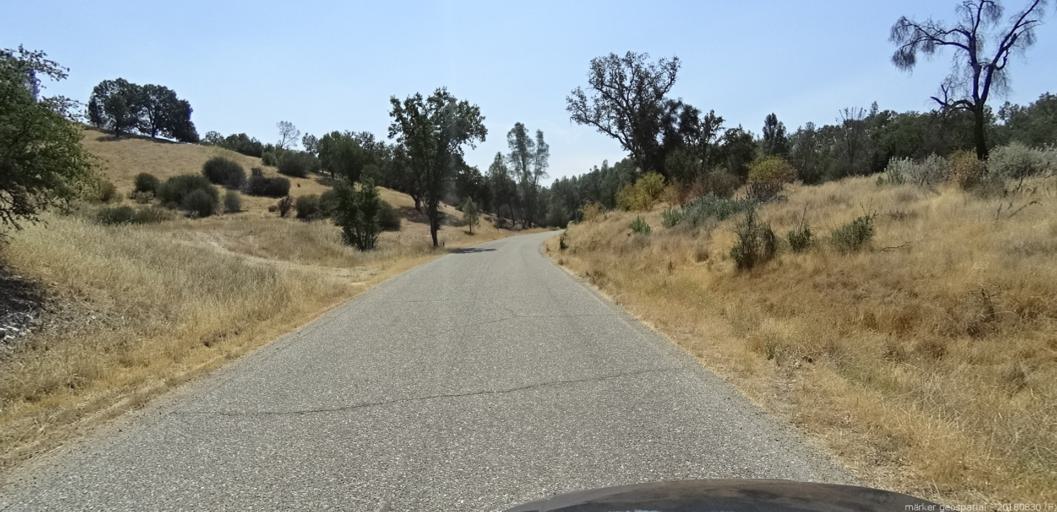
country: US
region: California
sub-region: Monterey County
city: King City
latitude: 35.9919
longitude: -121.2627
